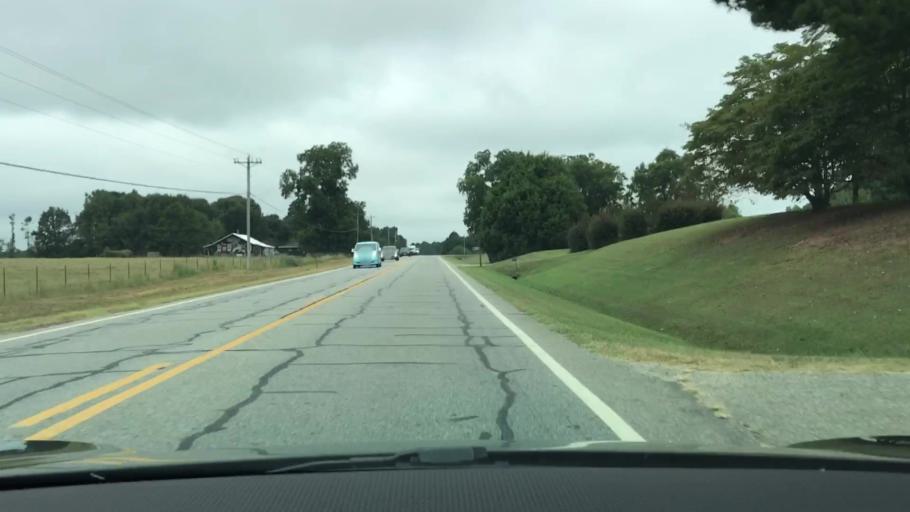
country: US
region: Georgia
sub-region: Oconee County
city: Watkinsville
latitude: 33.8023
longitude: -83.3401
